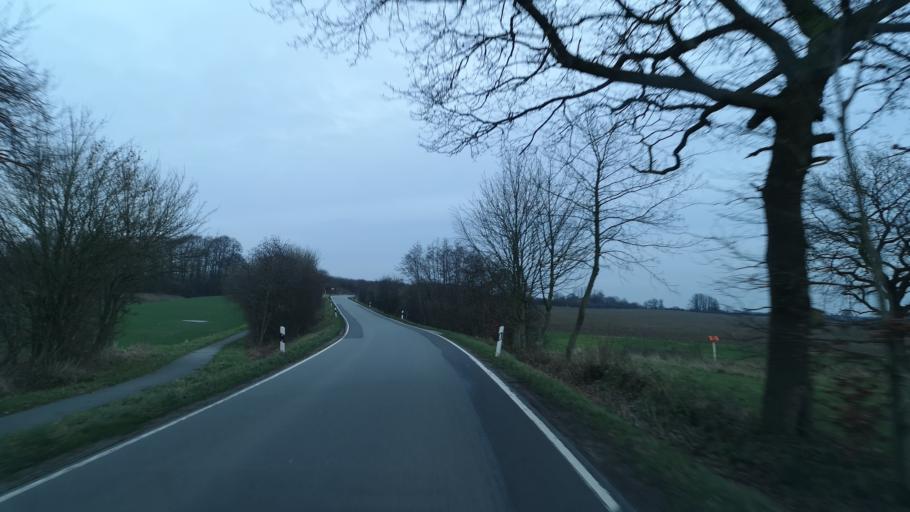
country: DE
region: Schleswig-Holstein
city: Satrup
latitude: 54.6973
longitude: 9.6182
